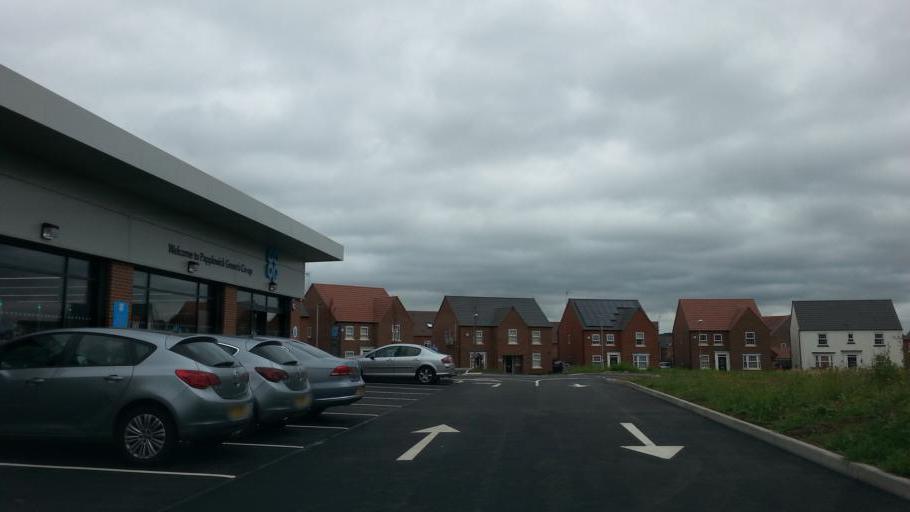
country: GB
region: England
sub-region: Nottinghamshire
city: Hucknall
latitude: 53.0419
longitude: -1.1911
